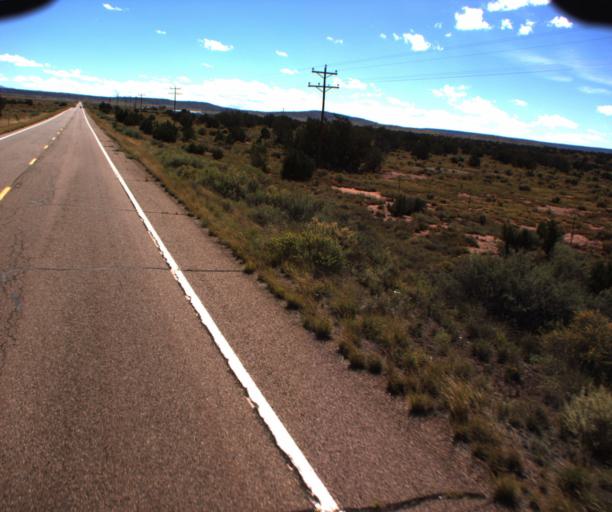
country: US
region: Arizona
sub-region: Apache County
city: Saint Johns
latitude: 34.5245
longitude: -109.6205
